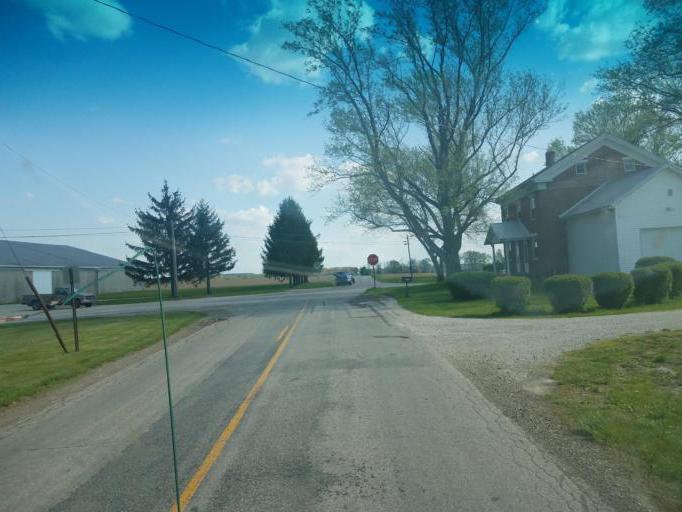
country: US
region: Ohio
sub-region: Wayne County
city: Smithville
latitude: 40.8500
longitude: -81.8779
